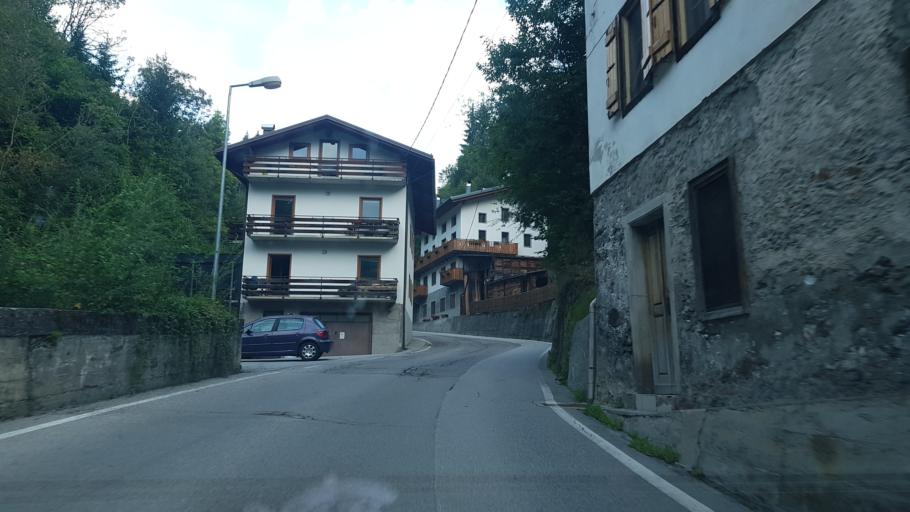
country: IT
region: Veneto
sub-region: Provincia di Belluno
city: San Pietro di Cadore
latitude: 46.5685
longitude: 12.5860
